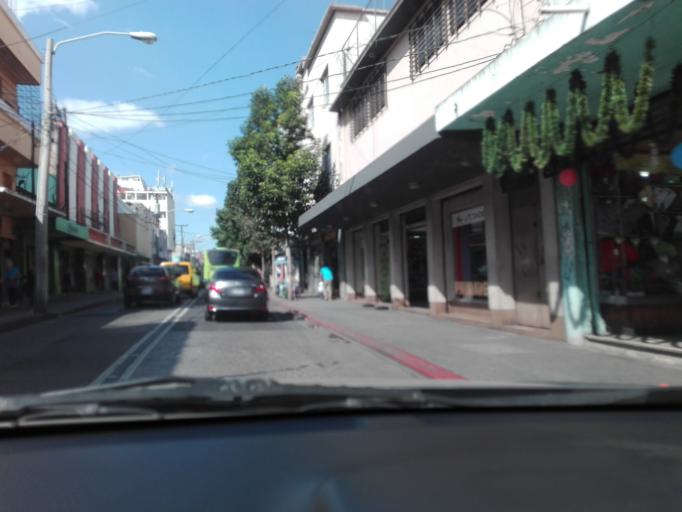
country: GT
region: Guatemala
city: Guatemala City
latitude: 14.6327
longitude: -90.5160
